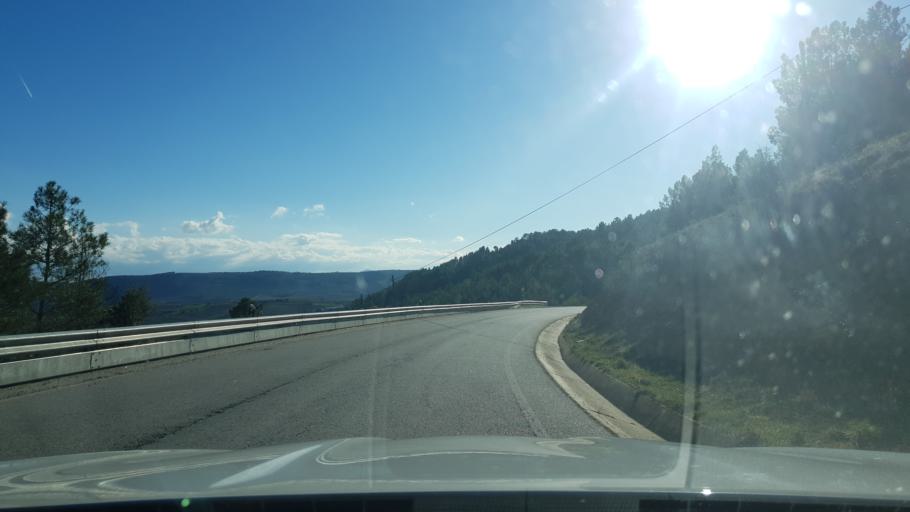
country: PT
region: Braganca
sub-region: Freixo de Espada A Cinta
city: Freixo de Espada a Cinta
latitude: 41.1094
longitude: -6.8245
